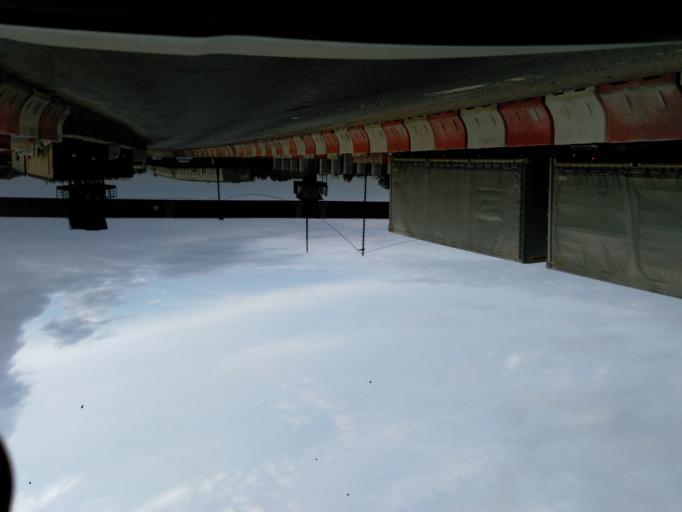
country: RU
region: Moskovskaya
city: Novopodrezkovo
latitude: 55.9706
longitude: 37.3741
